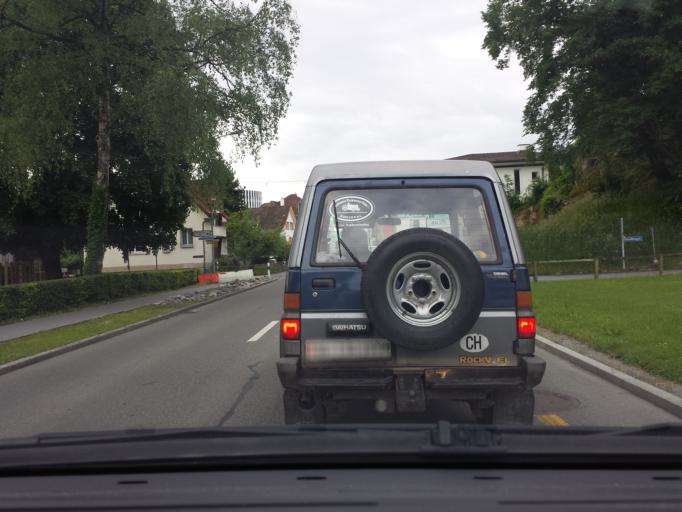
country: CH
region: Appenzell Innerrhoden
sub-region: Appenzell Inner Rhodes
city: Balgach
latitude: 47.4131
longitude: 9.6251
